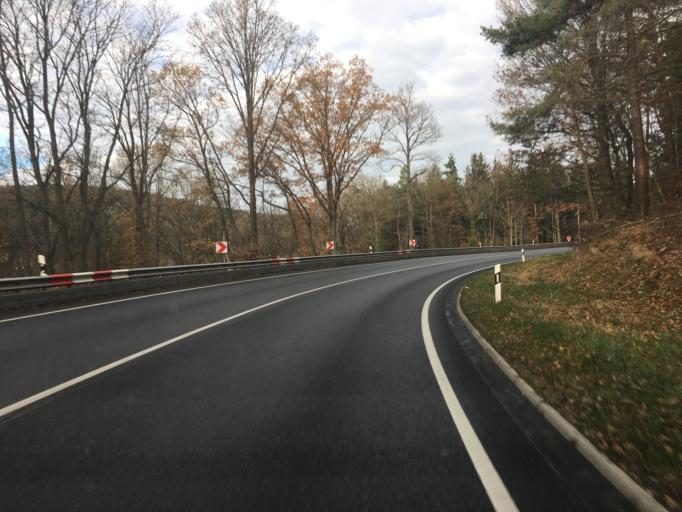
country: DE
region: North Rhine-Westphalia
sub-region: Regierungsbezirk Koln
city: Kall
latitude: 50.5549
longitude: 6.5426
